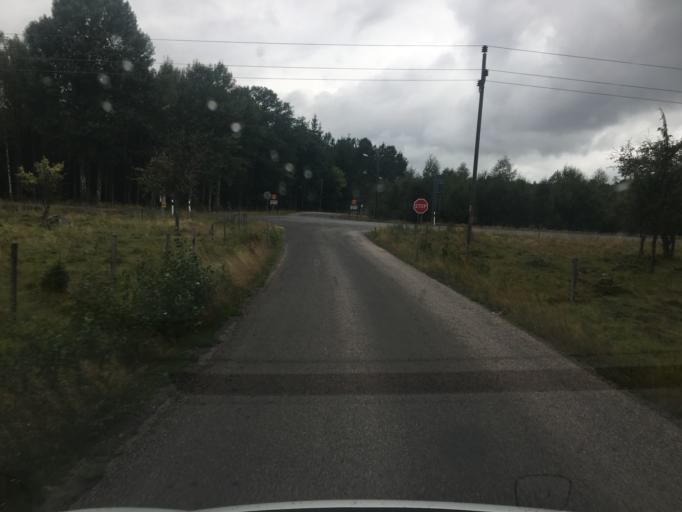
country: SE
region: Kronoberg
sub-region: Ljungby Kommun
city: Lagan
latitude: 56.9886
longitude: 14.0118
